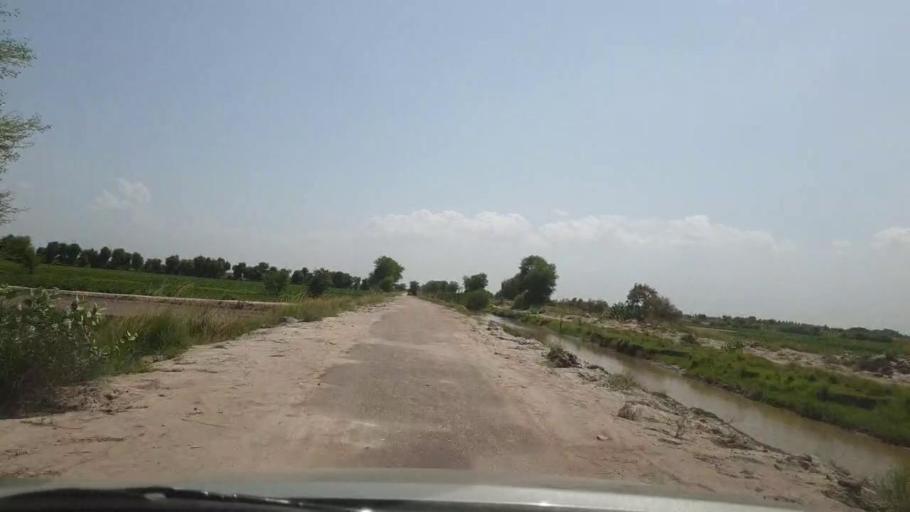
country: PK
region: Sindh
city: Pano Aqil
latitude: 27.7227
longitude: 69.0870
